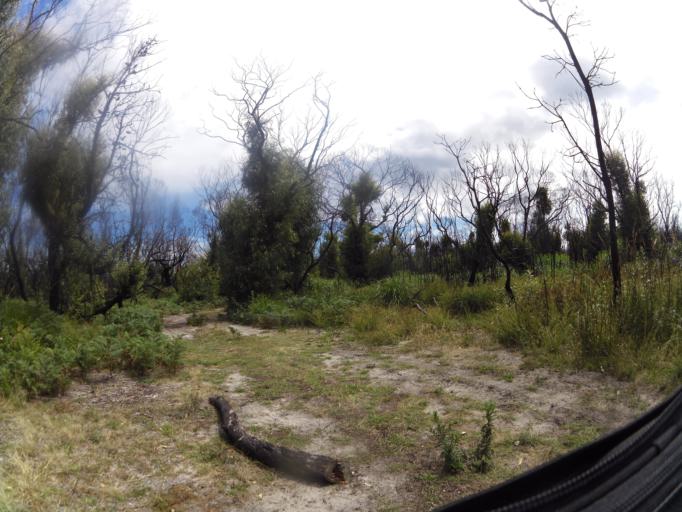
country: AU
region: Victoria
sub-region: East Gippsland
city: Lakes Entrance
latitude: -37.8013
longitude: 148.7400
